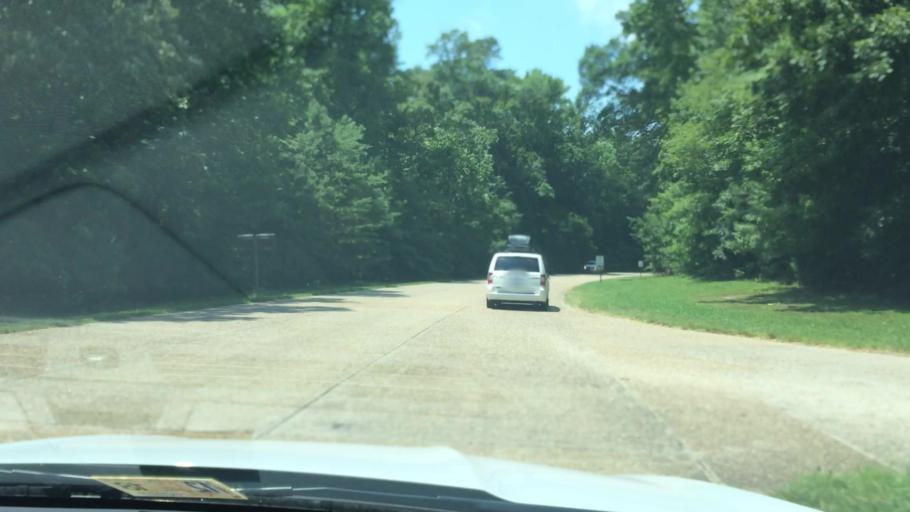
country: US
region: Virginia
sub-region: York County
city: Yorktown
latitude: 37.2290
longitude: -76.5177
